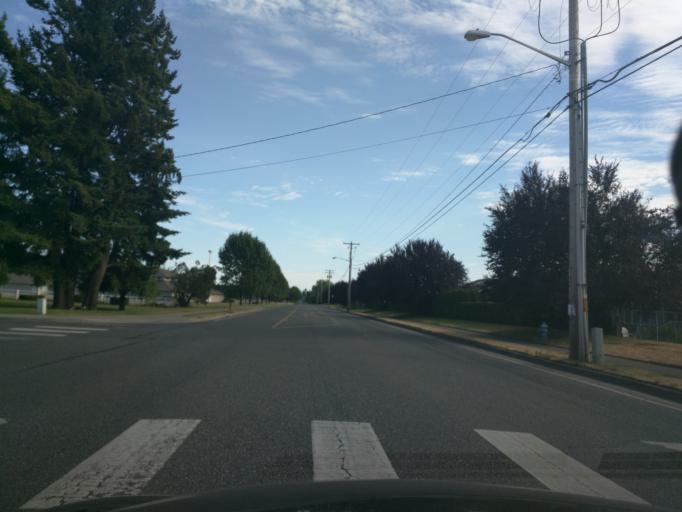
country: US
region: Washington
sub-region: Whatcom County
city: Lynden
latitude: 48.9627
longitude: -122.4412
